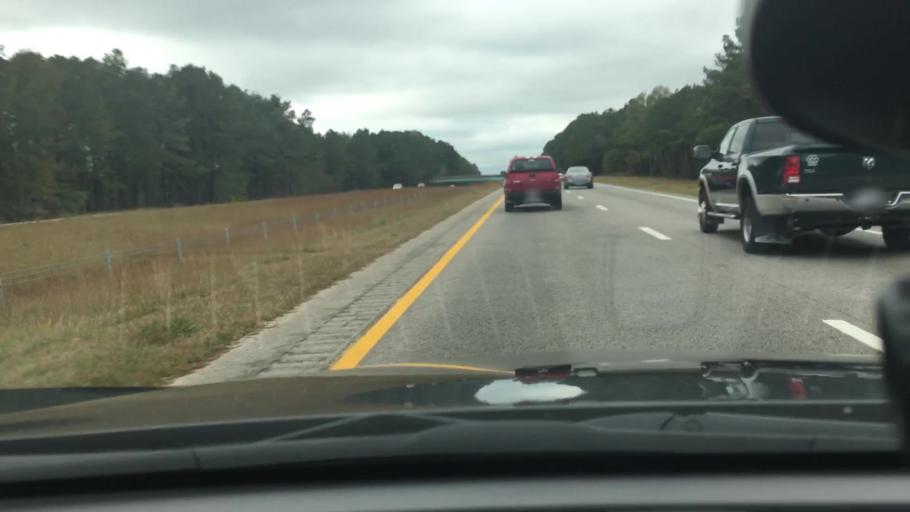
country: US
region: North Carolina
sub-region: Wake County
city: Zebulon
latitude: 35.8089
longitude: -78.2186
